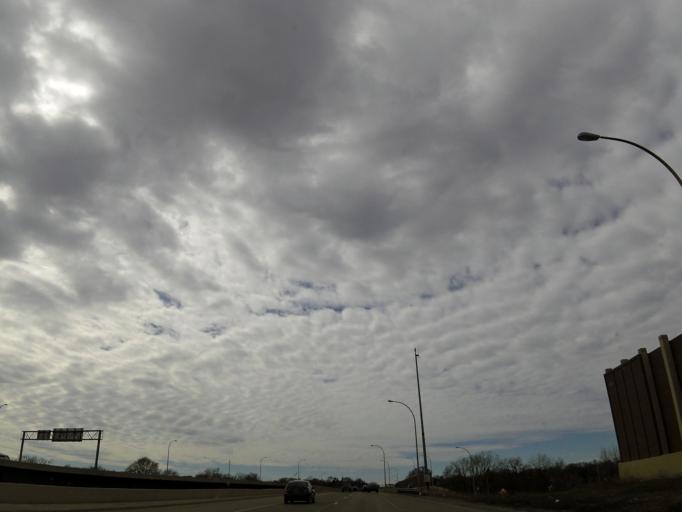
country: US
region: Minnesota
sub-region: Hennepin County
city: Richfield
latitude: 44.8906
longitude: -93.2933
